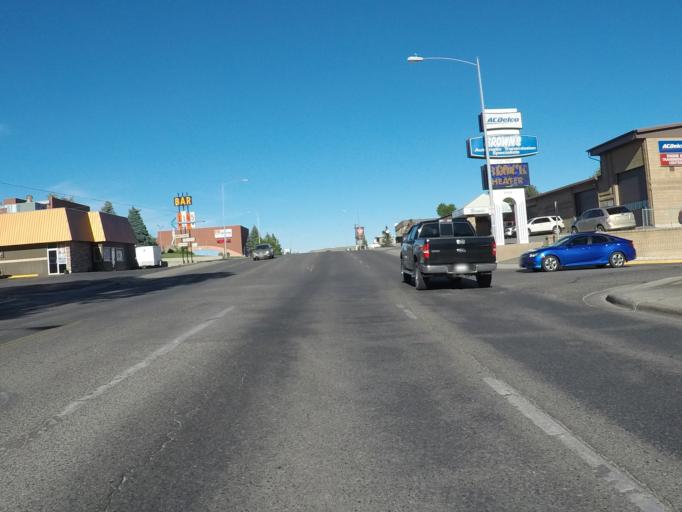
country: US
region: Montana
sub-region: Yellowstone County
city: Billings
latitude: 45.7770
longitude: -108.5464
